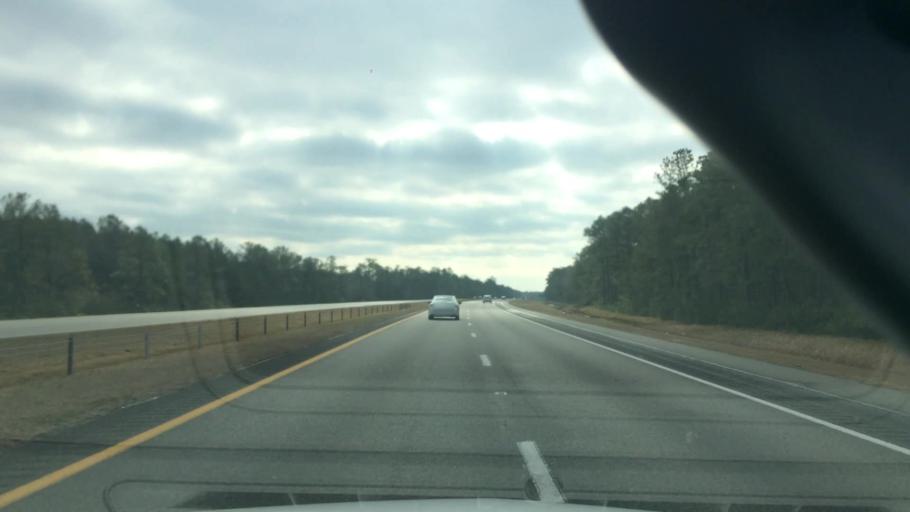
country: US
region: North Carolina
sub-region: New Hanover County
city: Castle Hayne
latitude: 34.3898
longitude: -77.8760
